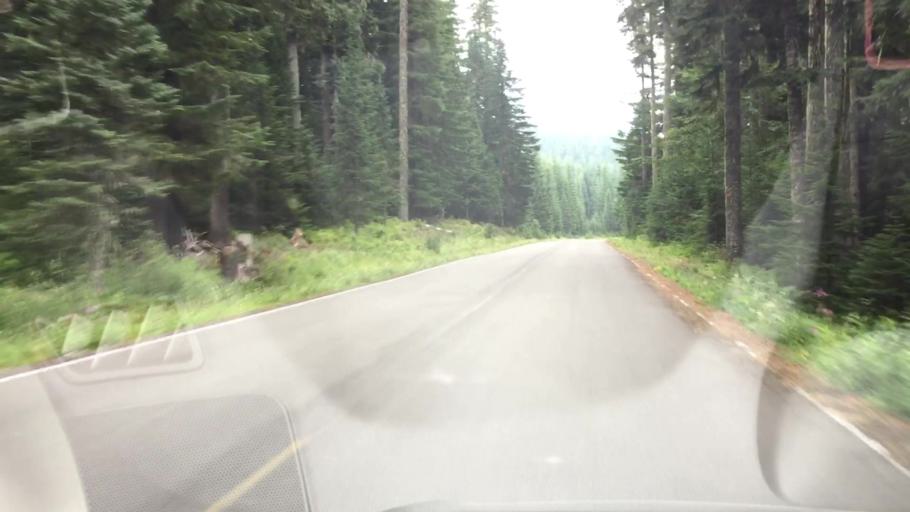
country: US
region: Washington
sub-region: Klickitat County
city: White Salmon
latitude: 46.1809
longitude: -121.6364
